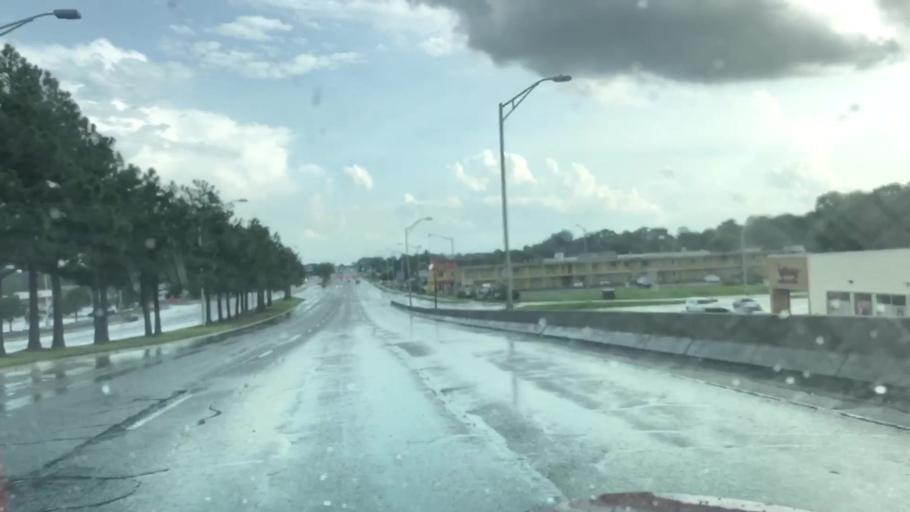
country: US
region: Virginia
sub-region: City of Chesapeake
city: Chesapeake
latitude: 36.8548
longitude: -76.2101
